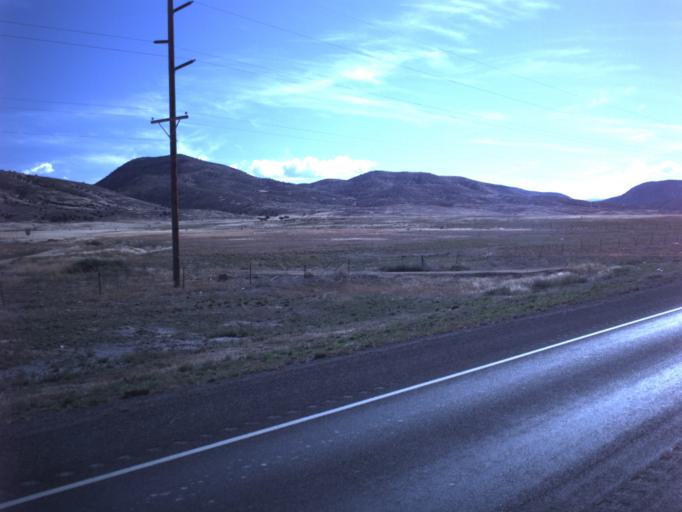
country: US
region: Utah
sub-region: Sanpete County
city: Gunnison
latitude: 39.2531
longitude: -111.8596
